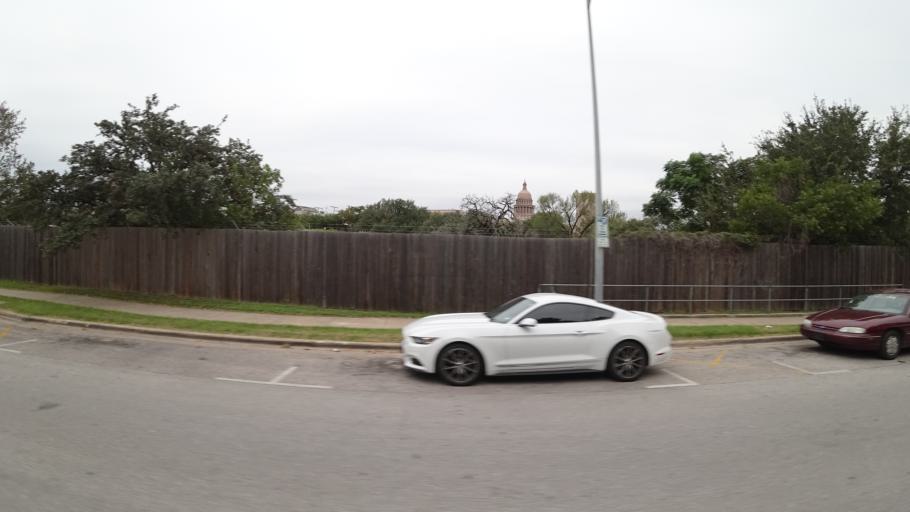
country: US
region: Texas
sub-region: Travis County
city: Austin
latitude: 30.2745
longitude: -97.7352
